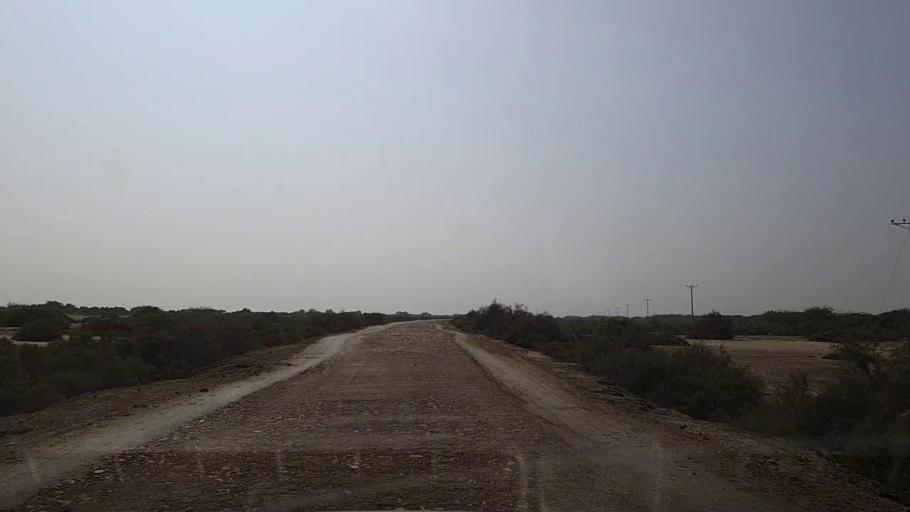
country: PK
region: Sindh
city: Mirpur Sakro
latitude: 24.5340
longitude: 67.5942
